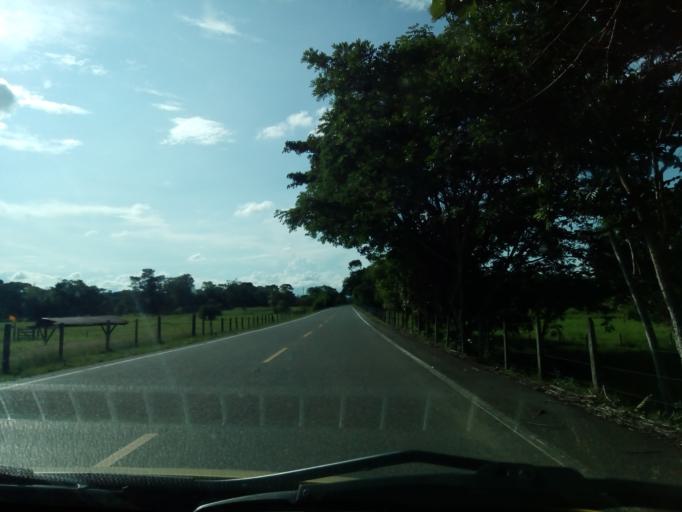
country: CO
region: Boyaca
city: Puerto Boyaca
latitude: 5.9358
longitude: -74.5480
